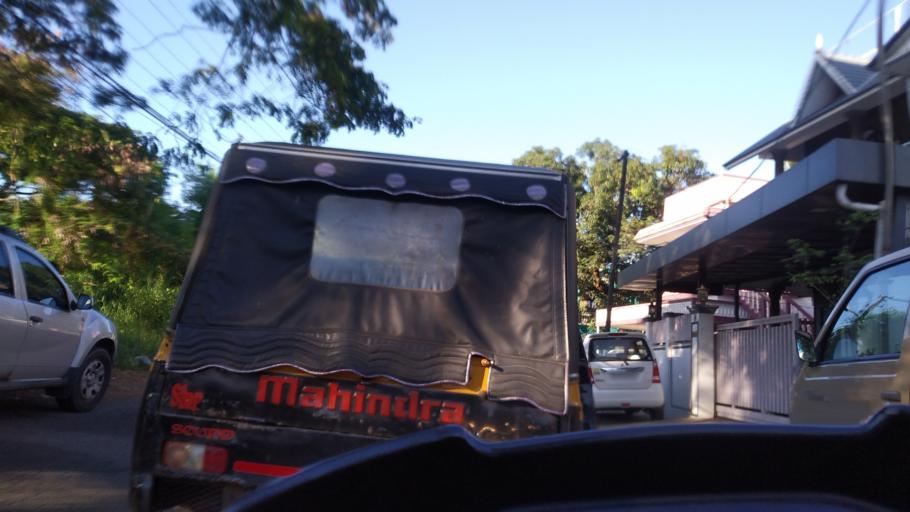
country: IN
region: Kerala
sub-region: Ernakulam
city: Cochin
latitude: 9.9990
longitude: 76.2787
